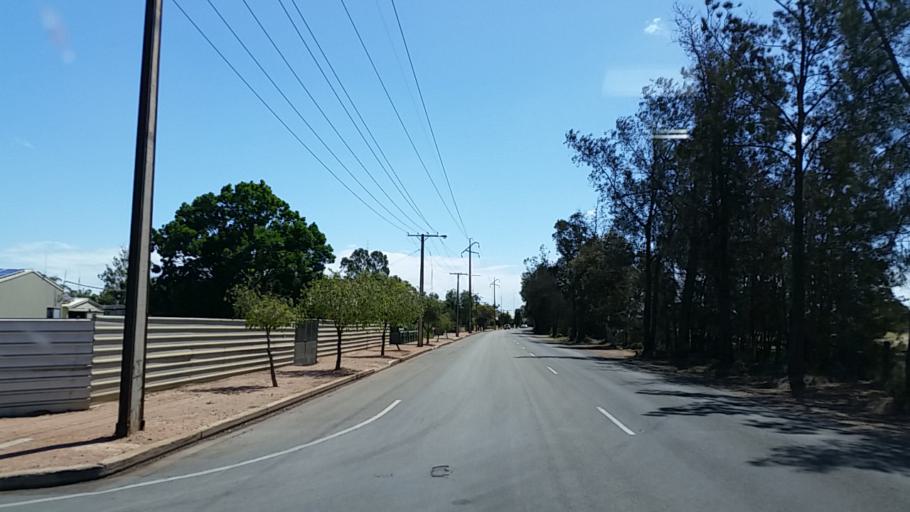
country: AU
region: South Australia
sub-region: Port Pirie City and Dists
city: Port Pirie
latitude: -33.1918
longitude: 138.0236
